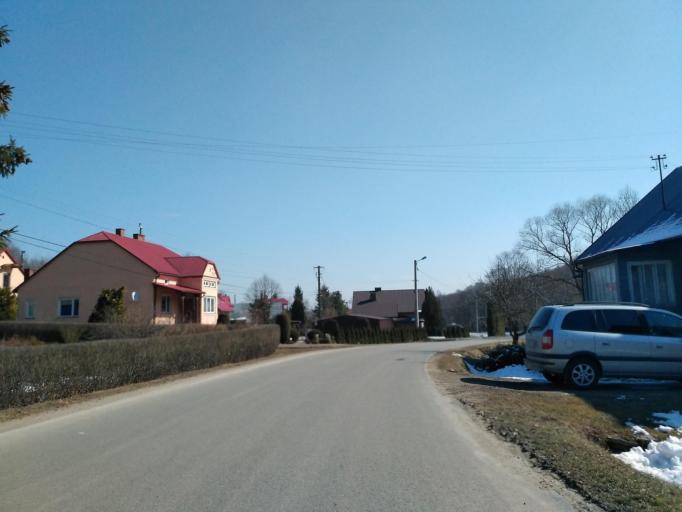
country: PL
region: Subcarpathian Voivodeship
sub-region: Powiat brzozowski
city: Jablonica Polska
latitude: 49.7537
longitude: 21.8814
